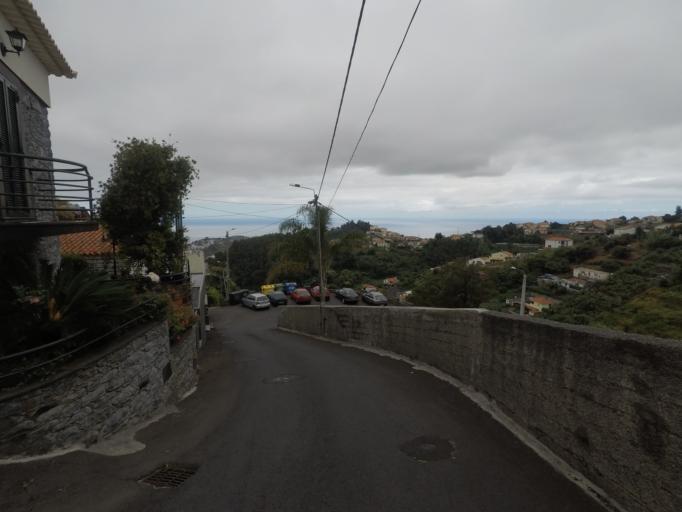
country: PT
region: Madeira
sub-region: Funchal
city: Nossa Senhora do Monte
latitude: 32.6764
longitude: -16.9435
